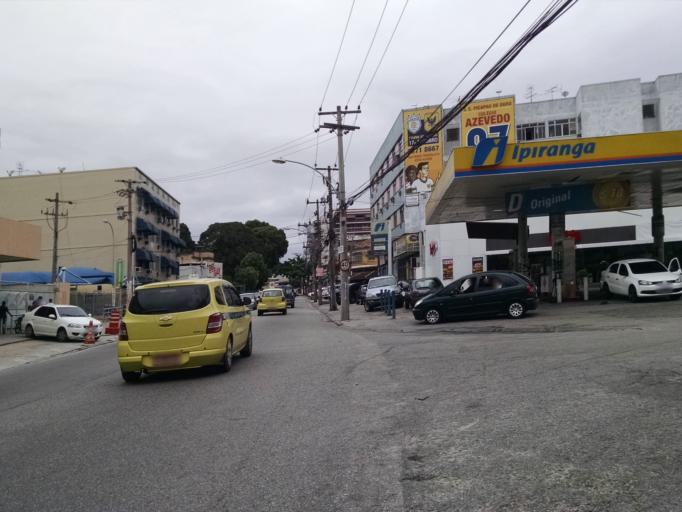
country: BR
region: Rio de Janeiro
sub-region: Duque De Caxias
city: Duque de Caxias
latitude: -22.8347
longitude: -43.3187
